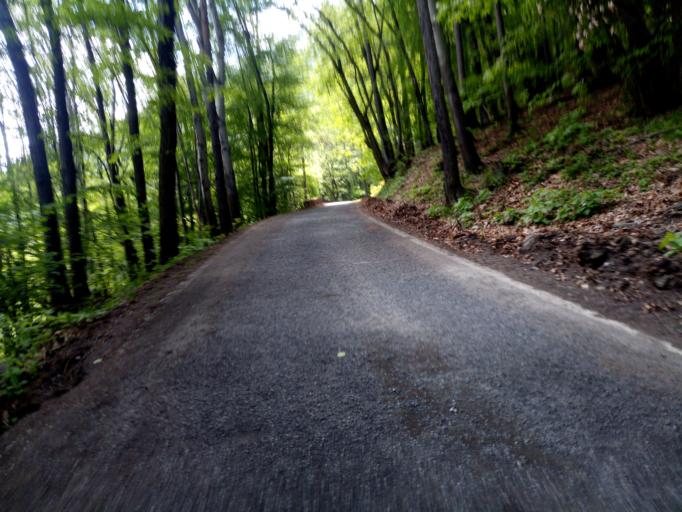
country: IT
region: Piedmont
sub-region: Provincia di Torino
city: Meana di Susa
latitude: 45.1120
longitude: 7.0609
